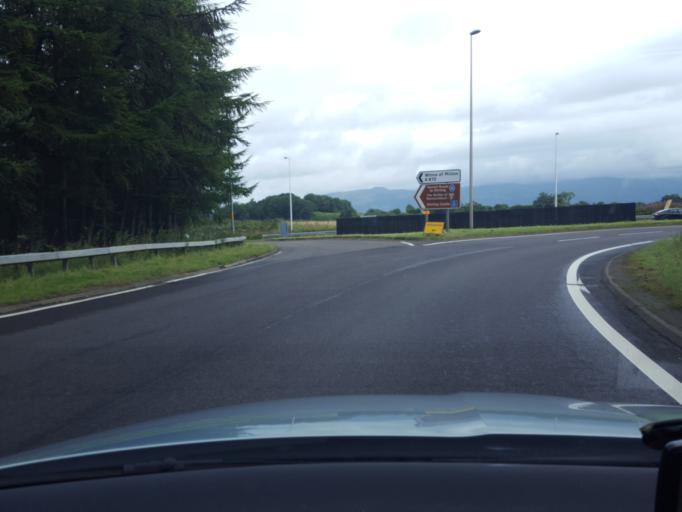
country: GB
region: Scotland
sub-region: Stirling
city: Bannockburn
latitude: 56.0782
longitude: -3.9216
